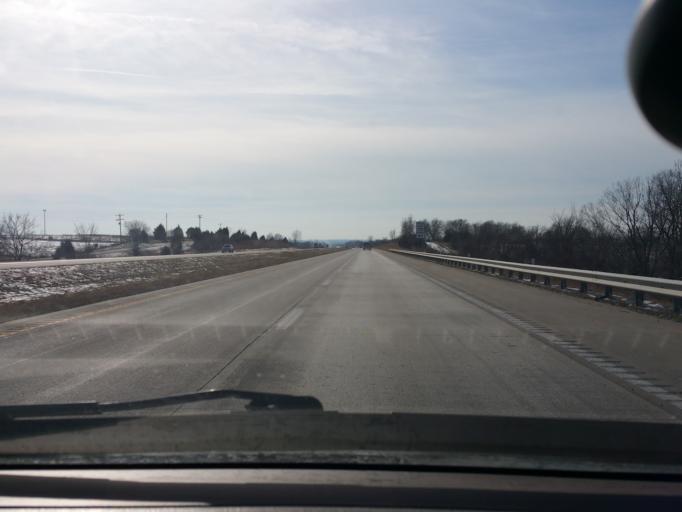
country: US
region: Missouri
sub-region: Clay County
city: Kearney
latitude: 39.4539
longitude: -94.3249
